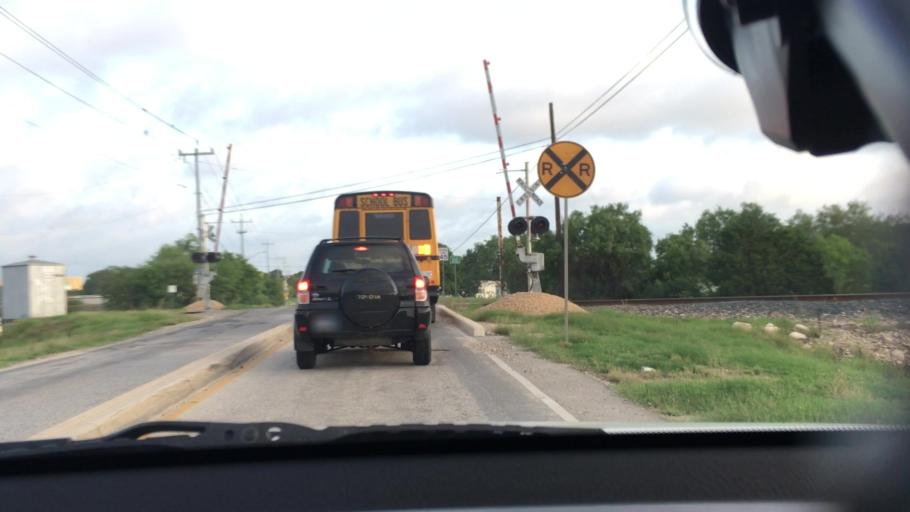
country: US
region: Texas
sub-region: Bexar County
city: Selma
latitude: 29.6074
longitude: -98.3310
